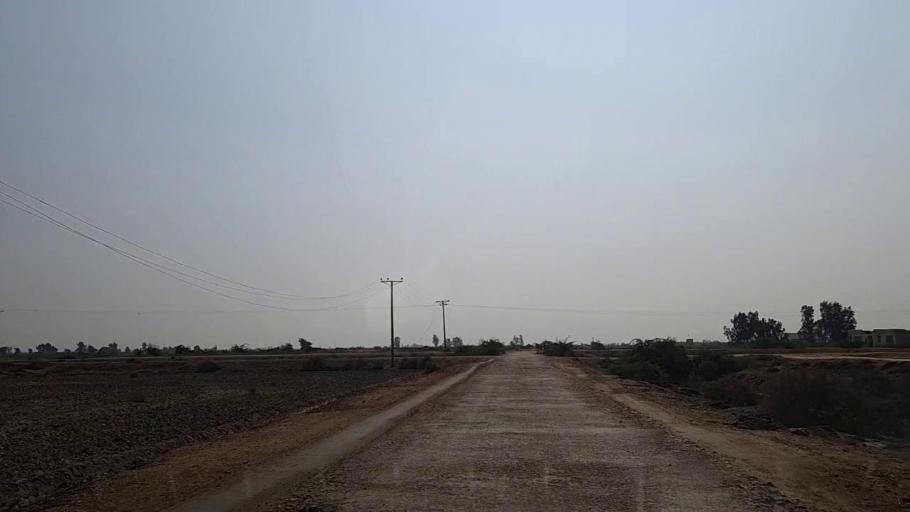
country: PK
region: Sindh
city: Thatta
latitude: 24.7123
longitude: 67.7685
